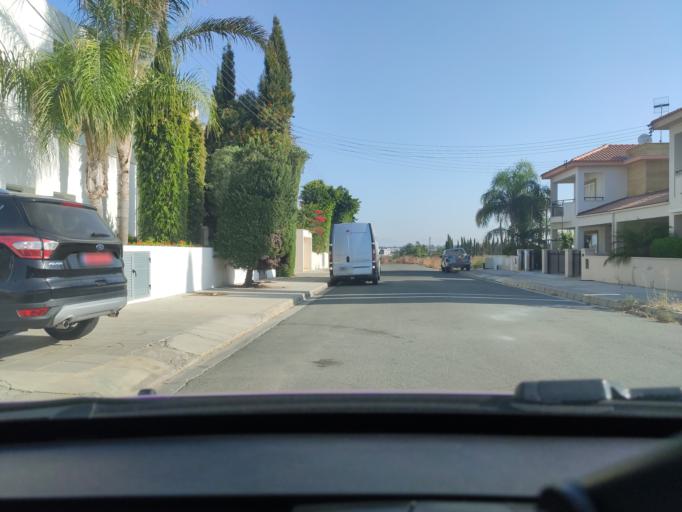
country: CY
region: Lefkosia
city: Tseri
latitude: 35.1097
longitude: 33.3512
